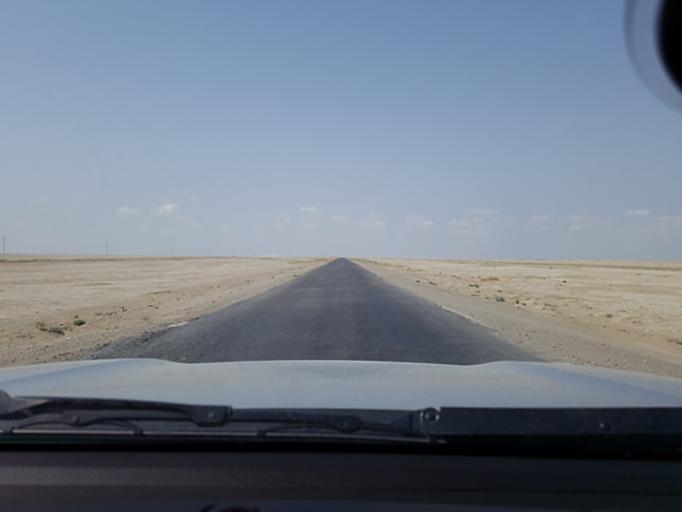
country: TM
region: Balkan
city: Gumdag
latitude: 38.6660
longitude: 54.4008
